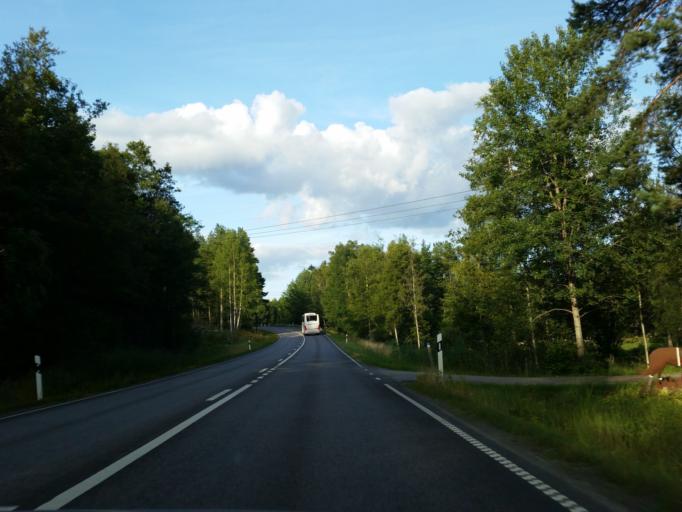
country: SE
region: Stockholm
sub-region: Sodertalje Kommun
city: Molnbo
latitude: 59.0642
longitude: 17.5181
